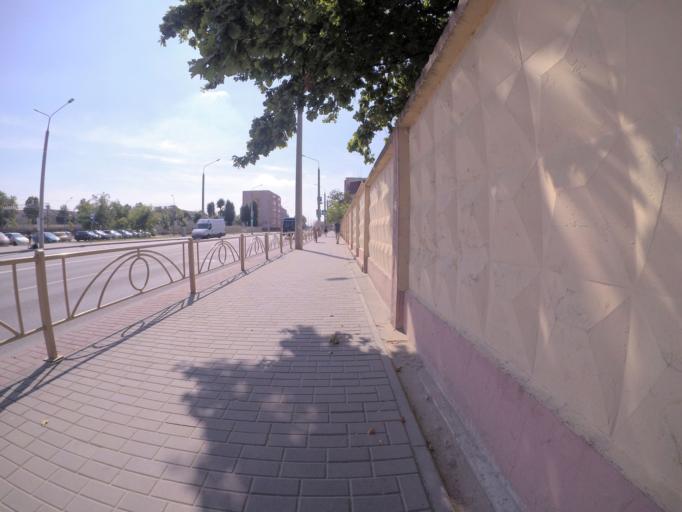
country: BY
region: Grodnenskaya
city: Hrodna
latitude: 53.6829
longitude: 23.8447
